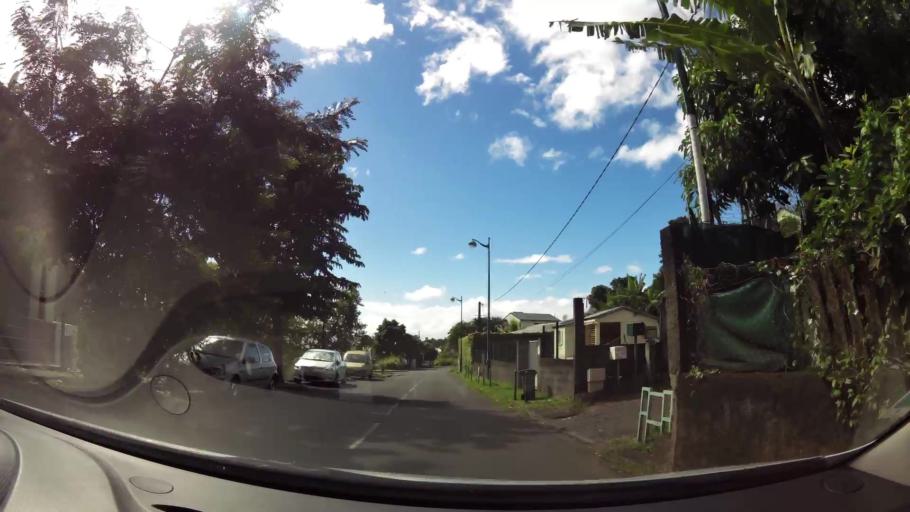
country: RE
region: Reunion
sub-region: Reunion
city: Saint-Denis
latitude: -20.9260
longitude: 55.4894
